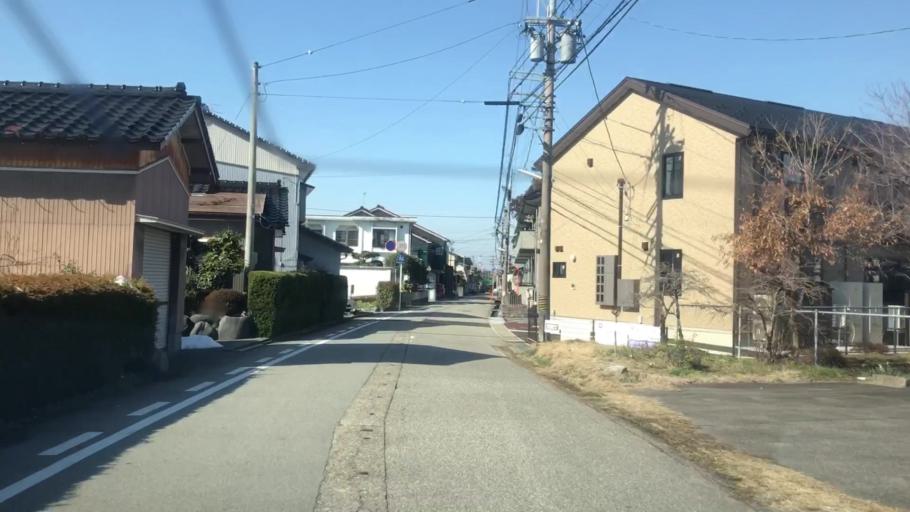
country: JP
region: Toyama
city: Toyama-shi
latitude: 36.6797
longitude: 137.2391
